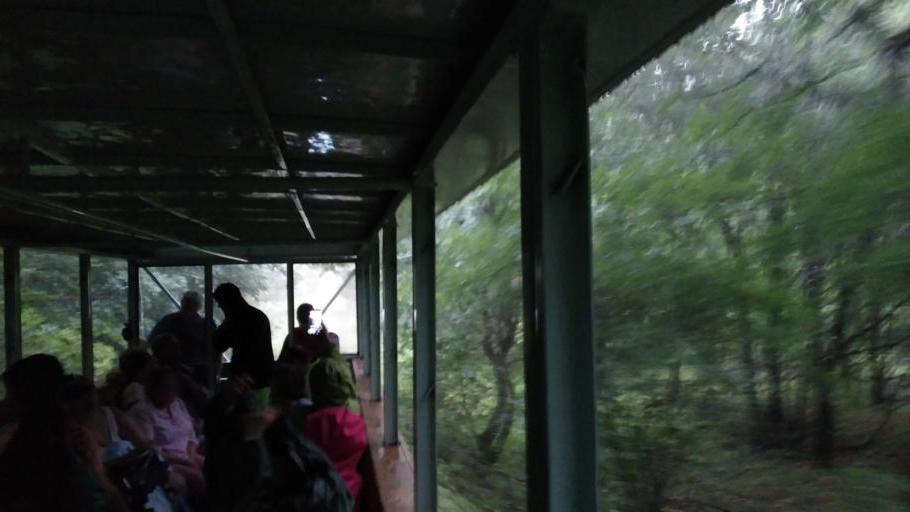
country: HU
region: Pest
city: Szob
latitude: 47.9275
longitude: 18.8461
